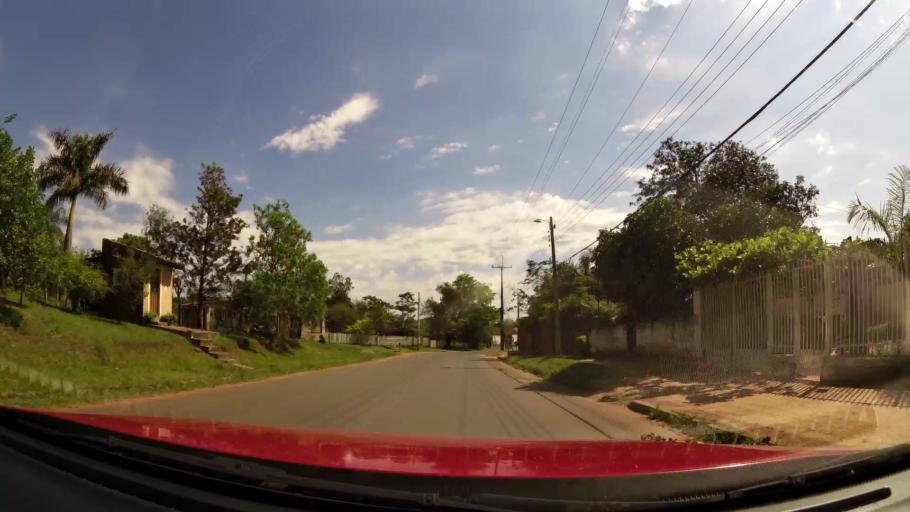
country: PY
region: Central
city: San Lorenzo
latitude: -25.2538
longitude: -57.4933
